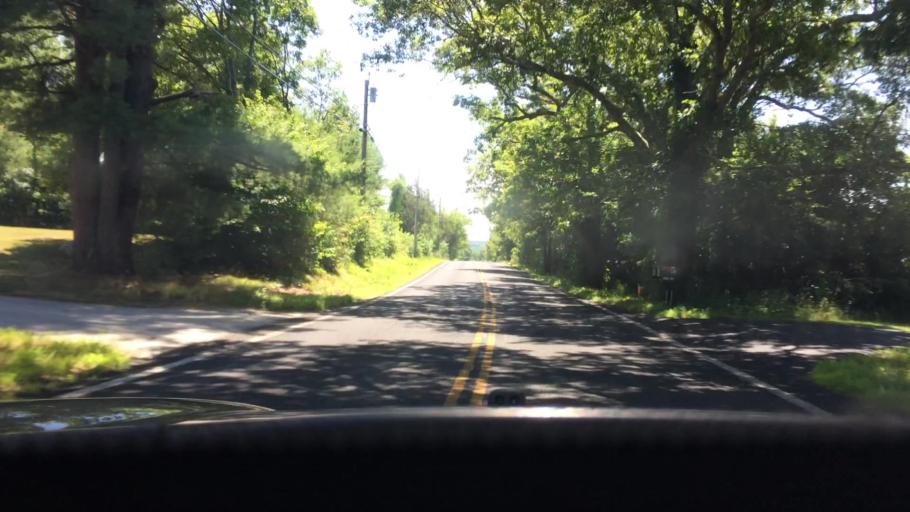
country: US
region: Rhode Island
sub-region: Providence County
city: Harrisville
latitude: 41.9789
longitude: -71.6827
